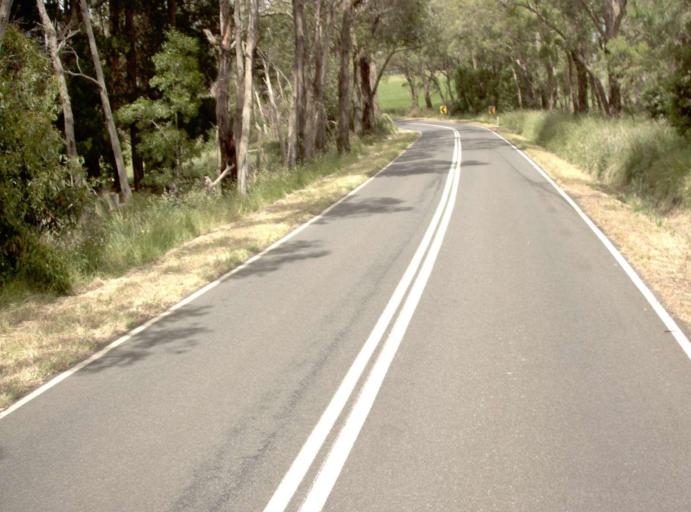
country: AU
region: Victoria
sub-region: Latrobe
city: Moe
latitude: -38.0743
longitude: 146.1722
